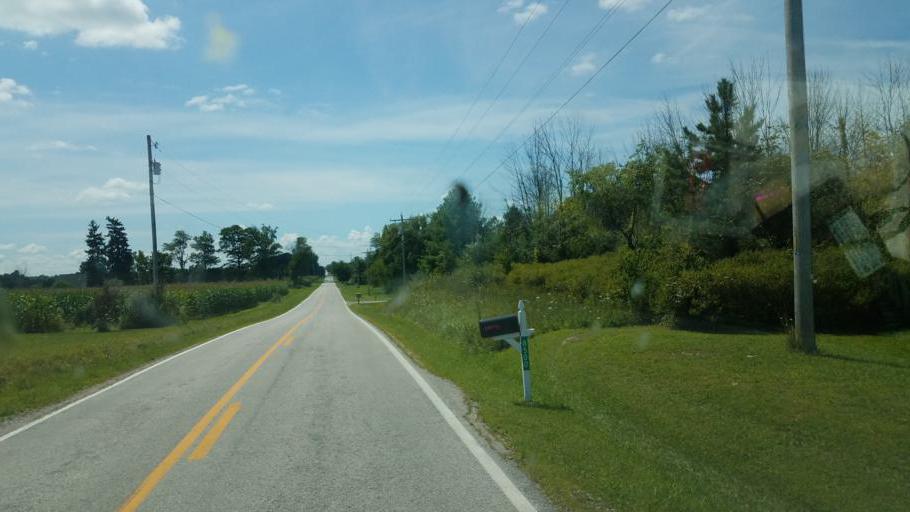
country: US
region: Ohio
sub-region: Knox County
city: Centerburg
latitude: 40.3354
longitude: -82.7941
